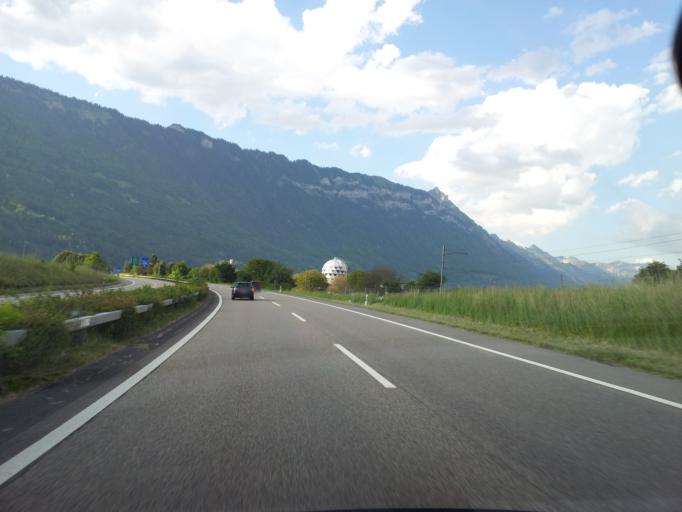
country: CH
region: Bern
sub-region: Interlaken-Oberhasli District
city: Matten
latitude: 46.6773
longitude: 7.8757
